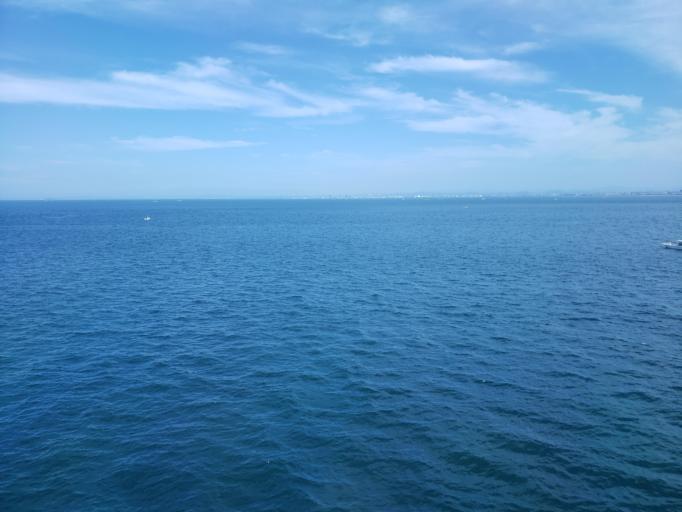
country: JP
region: Hyogo
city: Akashi
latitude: 34.6046
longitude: 134.9233
